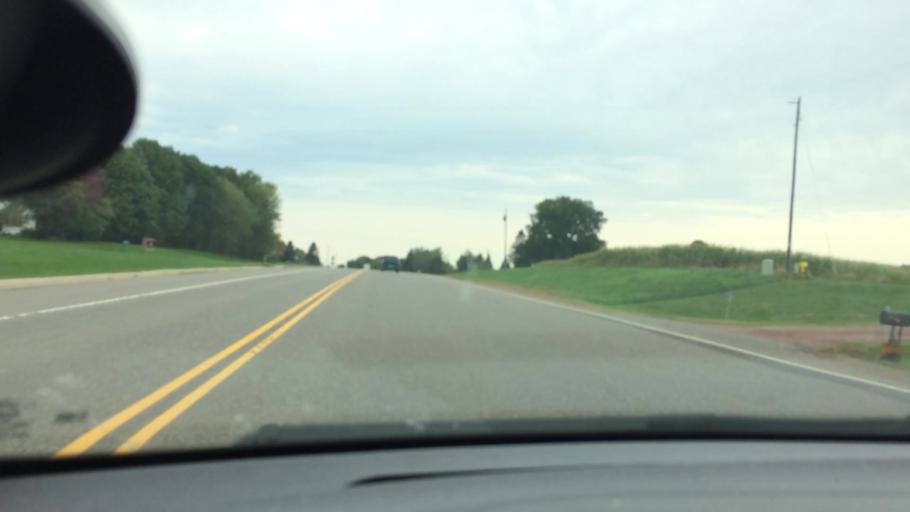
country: US
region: Wisconsin
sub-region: Clark County
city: Neillsville
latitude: 44.5600
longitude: -90.6450
